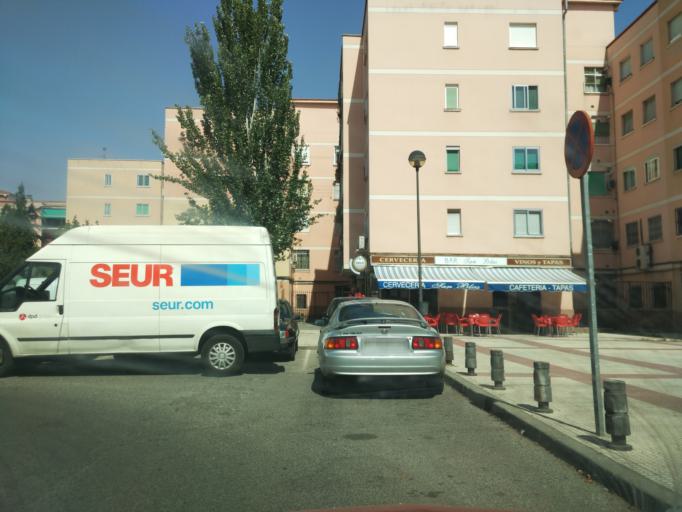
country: ES
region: Madrid
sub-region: Provincia de Madrid
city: Leganes
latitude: 40.3342
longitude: -3.7671
